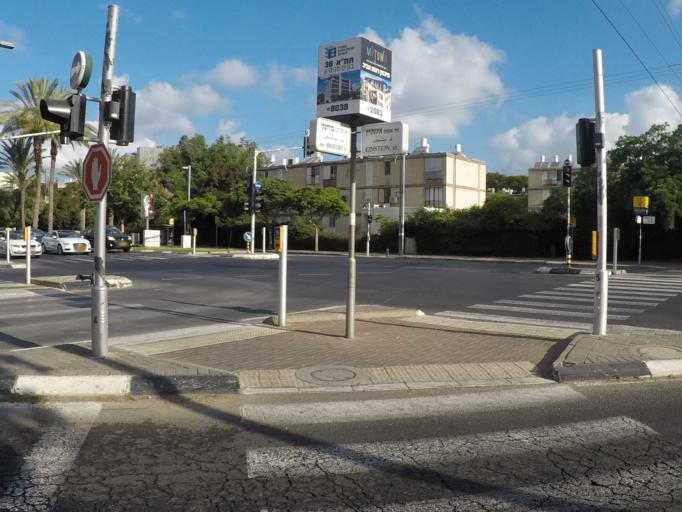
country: IL
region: Tel Aviv
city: Ramat Gan
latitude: 32.1129
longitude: 34.7979
